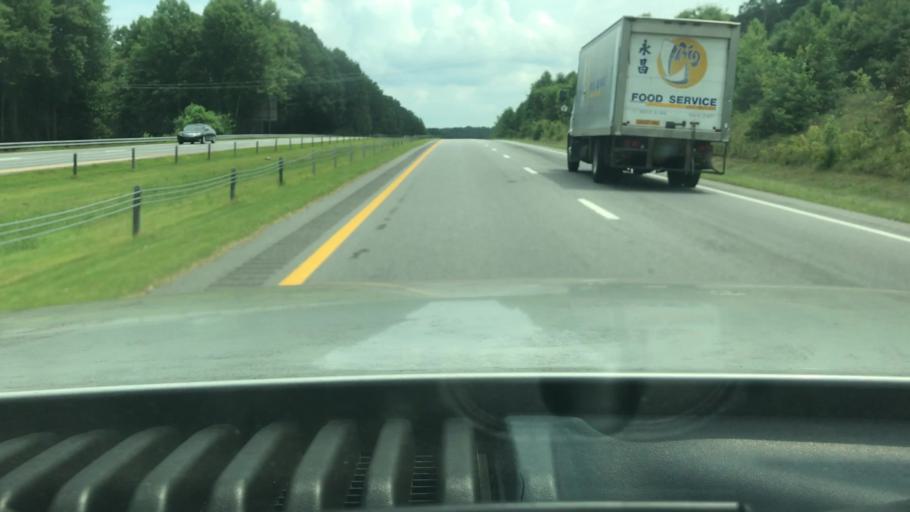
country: US
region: North Carolina
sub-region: Wilkes County
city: North Wilkesboro
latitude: 36.1421
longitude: -81.0660
